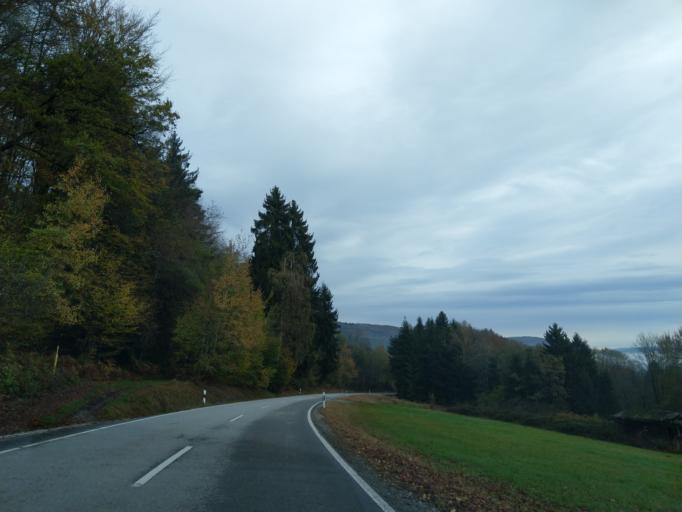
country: DE
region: Bavaria
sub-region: Lower Bavaria
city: Zenting
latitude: 48.7912
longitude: 13.2367
